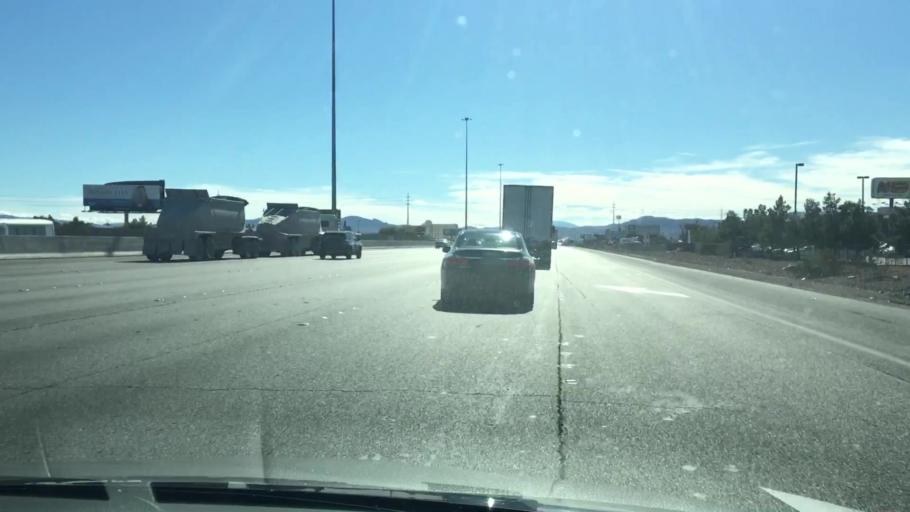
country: US
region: Nevada
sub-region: Clark County
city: Enterprise
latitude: 36.0396
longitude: -115.1811
